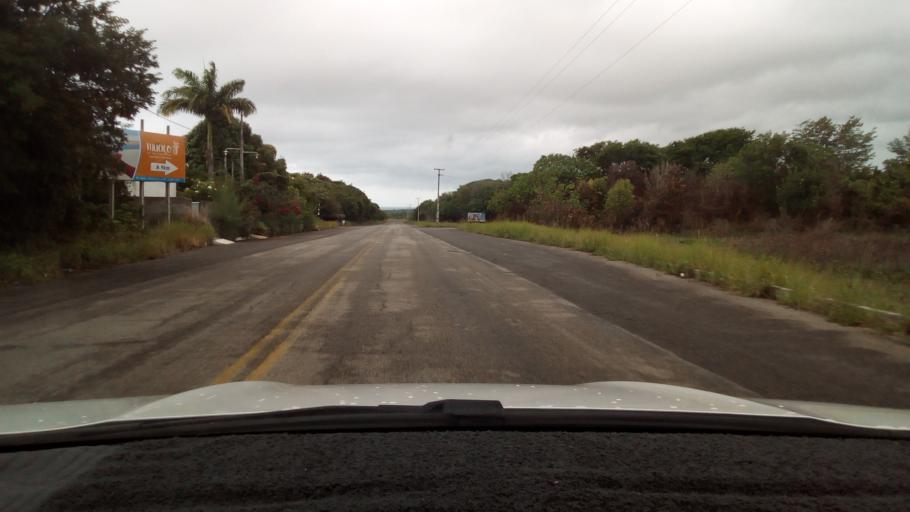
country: BR
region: Paraiba
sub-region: Pitimbu
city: Pitimbu
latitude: -7.3490
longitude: -34.8041
